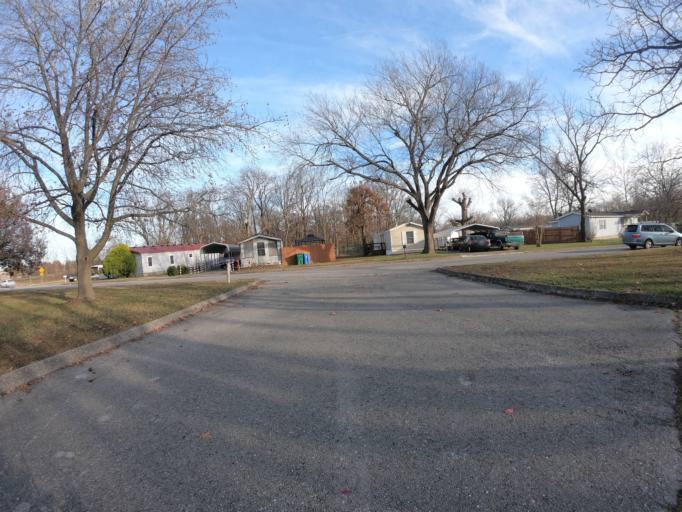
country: US
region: Arkansas
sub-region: Benton County
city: Rogers
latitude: 36.3330
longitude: -94.1702
